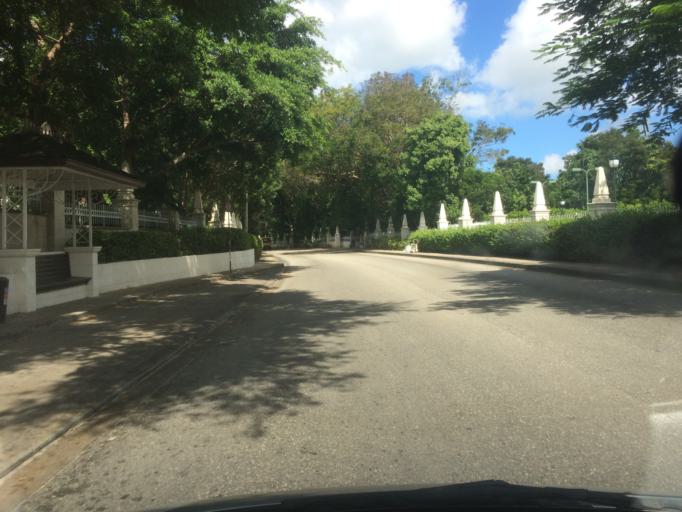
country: BB
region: Saint James
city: Holetown
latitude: 13.1732
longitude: -59.6357
